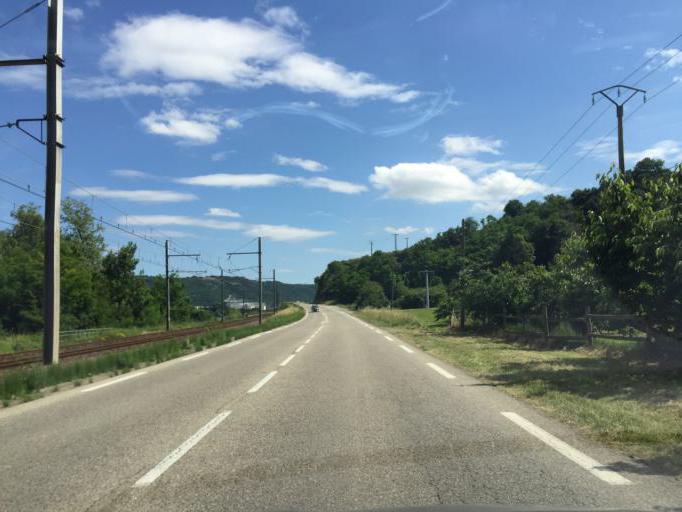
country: FR
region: Rhone-Alpes
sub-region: Departement de l'Ardeche
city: Andance
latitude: 45.2268
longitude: 4.8008
